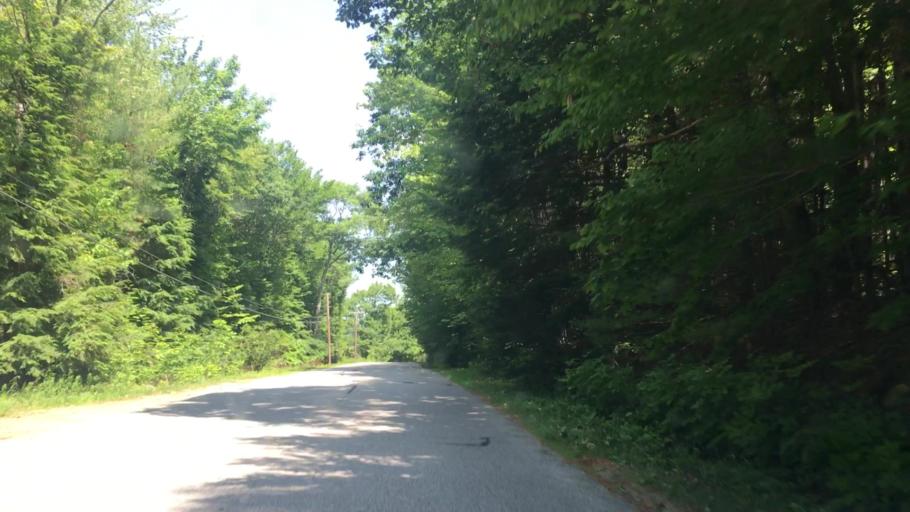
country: US
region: Maine
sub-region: Kennebec County
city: Wayne
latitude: 44.3268
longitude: -70.0591
